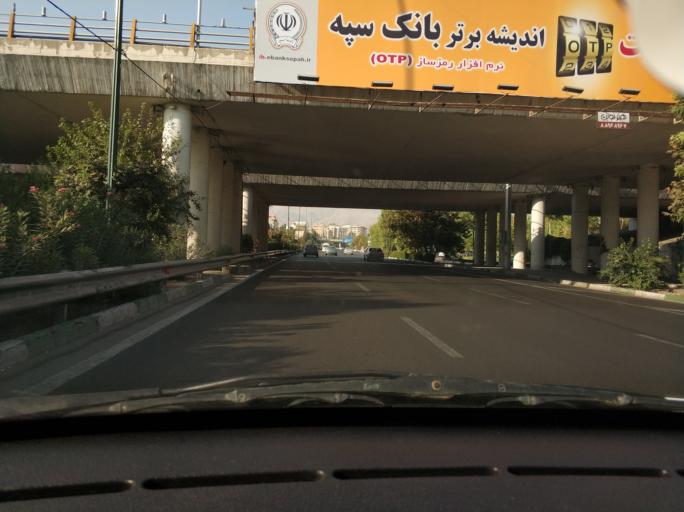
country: IR
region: Tehran
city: Tajrish
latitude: 35.7564
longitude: 51.4654
